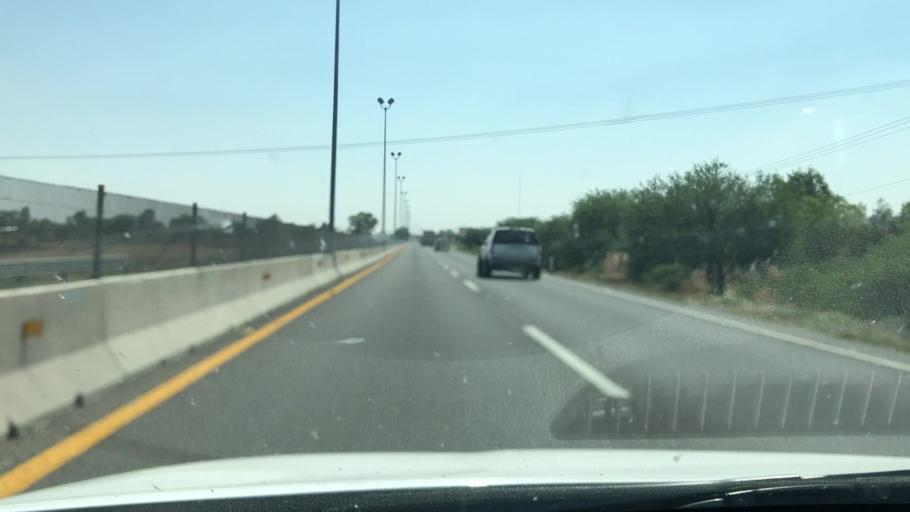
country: MX
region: Guanajuato
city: Abasolo
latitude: 20.4555
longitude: -101.5400
